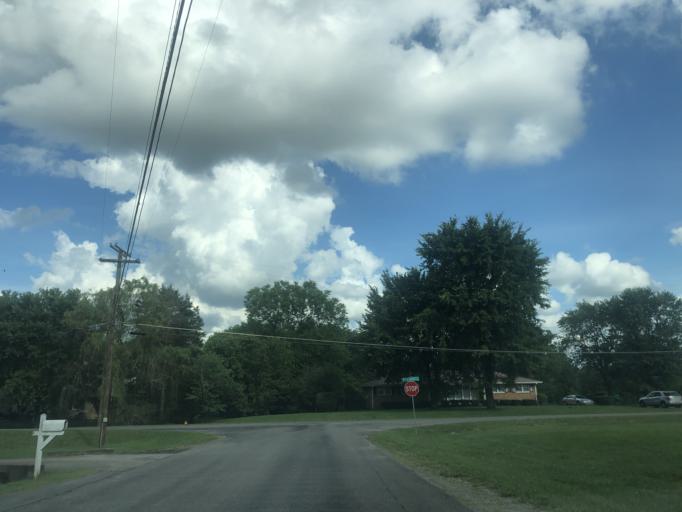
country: US
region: Tennessee
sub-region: Davidson County
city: Nashville
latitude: 36.2087
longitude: -86.8548
